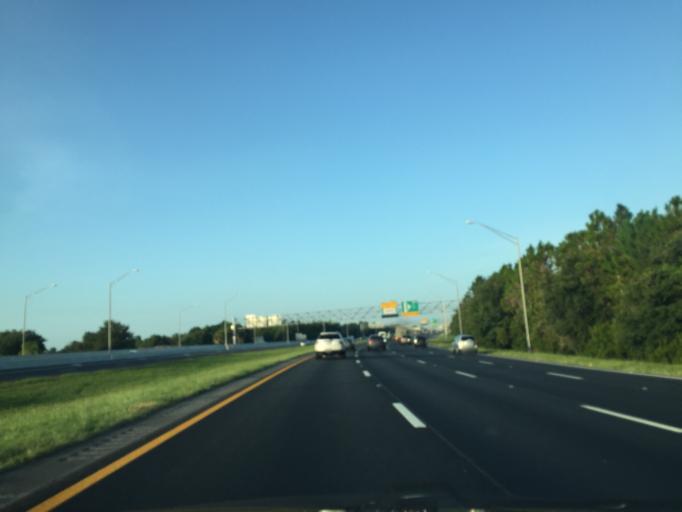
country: US
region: Florida
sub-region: Seminole County
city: Goldenrod
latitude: 28.5940
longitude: -81.2506
